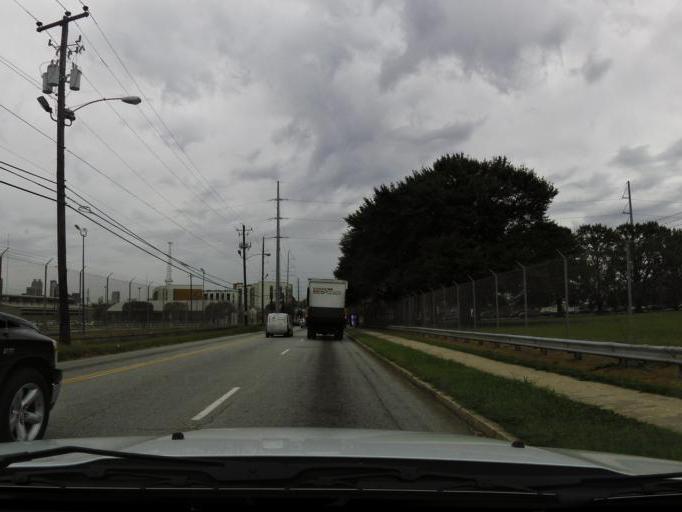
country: US
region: Georgia
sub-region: Fulton County
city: Atlanta
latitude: 33.7889
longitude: -84.4120
